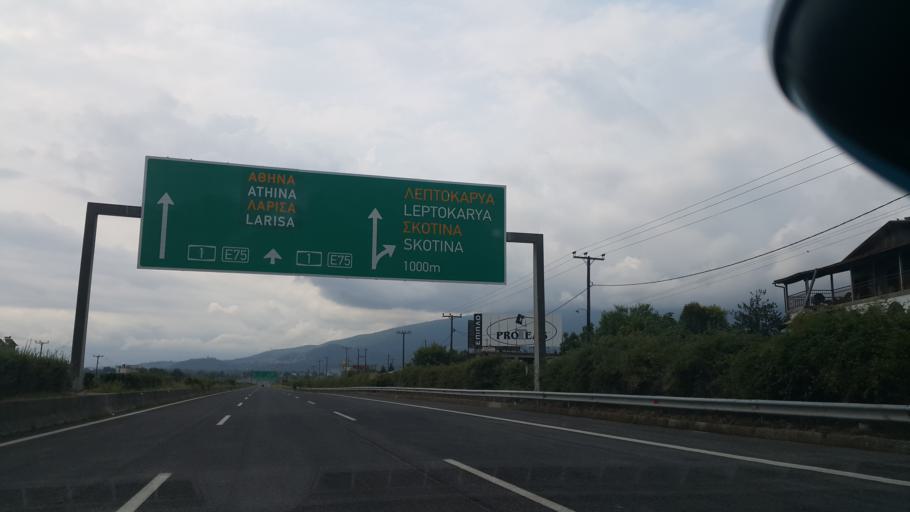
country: GR
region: Central Macedonia
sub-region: Nomos Pierias
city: Leptokarya
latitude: 40.0549
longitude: 22.5582
